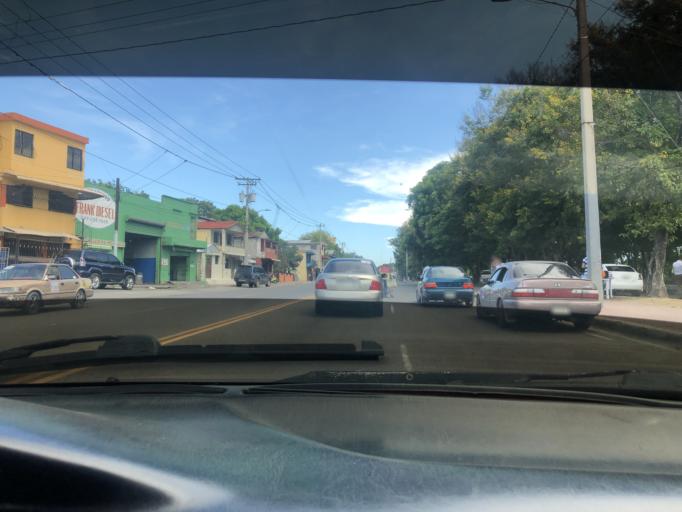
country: DO
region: Santiago
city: Santiago de los Caballeros
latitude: 19.4368
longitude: -70.6979
